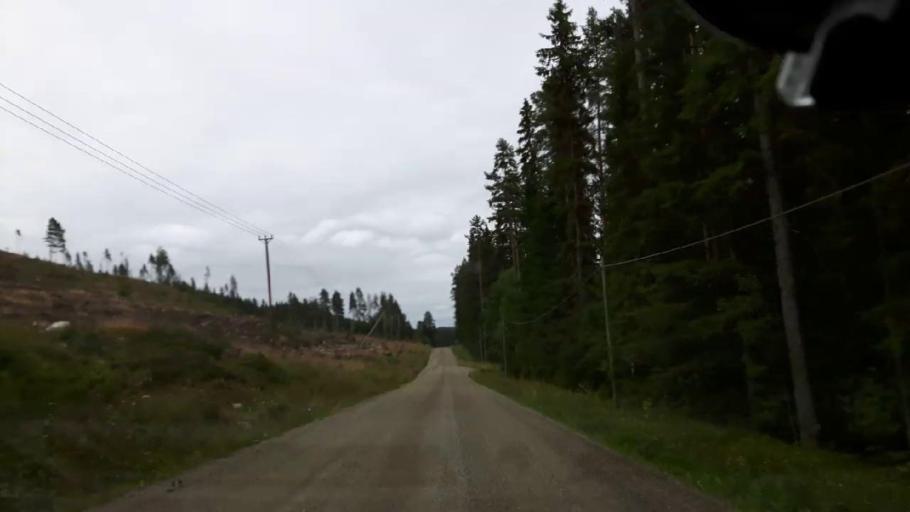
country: SE
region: Jaemtland
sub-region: Braecke Kommun
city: Braecke
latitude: 63.0430
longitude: 15.3559
